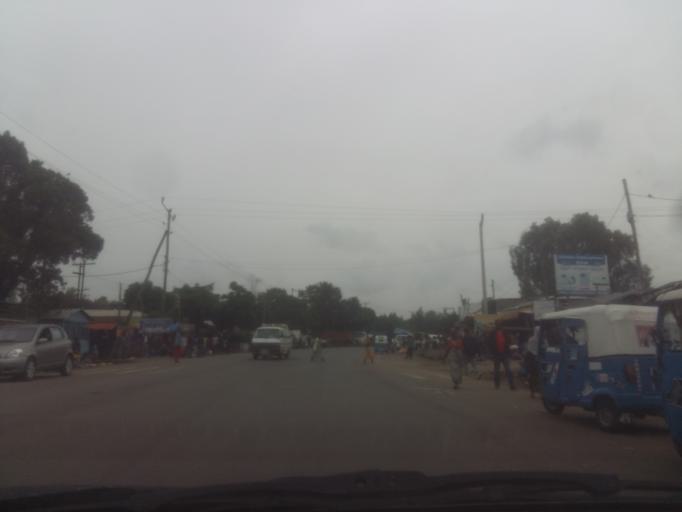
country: ET
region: Oromiya
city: Bishoftu
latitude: 8.7940
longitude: 38.9005
